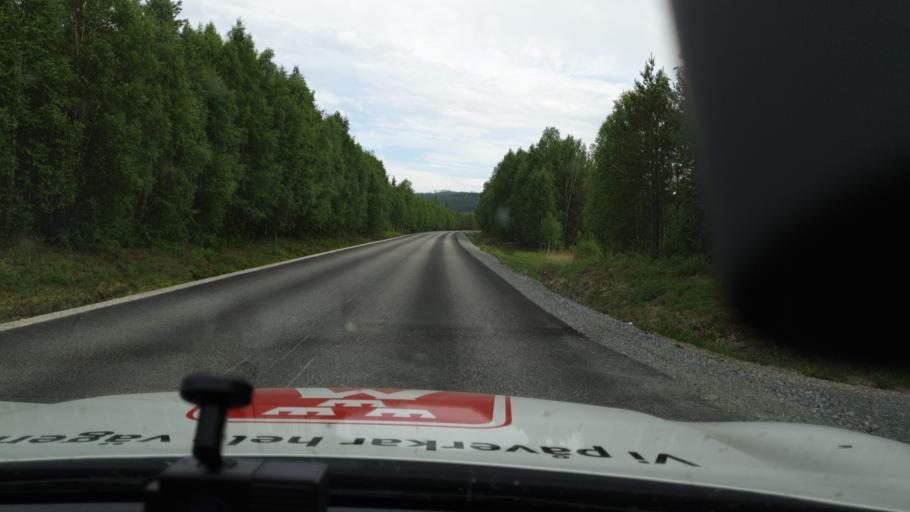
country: SE
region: Vaesterbotten
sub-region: Mala Kommun
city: Mala
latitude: 64.9302
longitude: 18.6190
